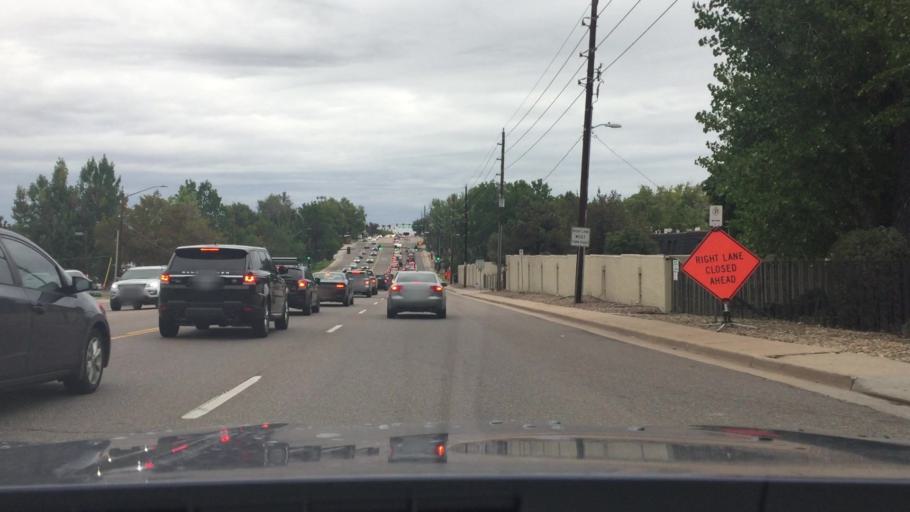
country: US
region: Colorado
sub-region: Arapahoe County
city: Southglenn
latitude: 39.5912
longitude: -104.9882
